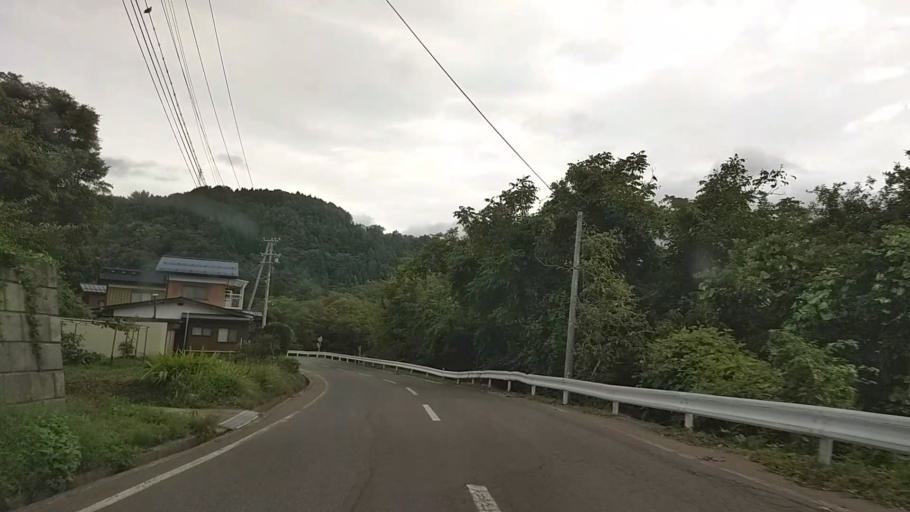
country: JP
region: Nagano
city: Nakano
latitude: 36.7861
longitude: 138.3335
